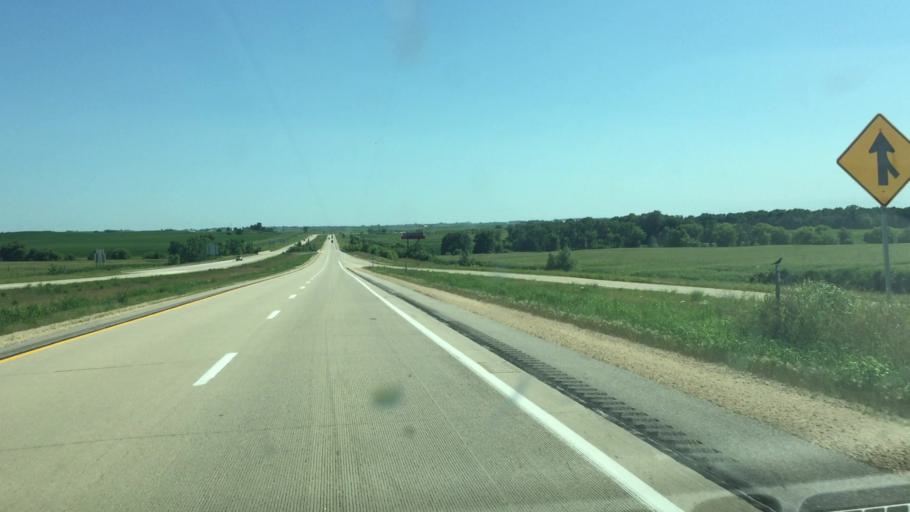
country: US
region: Iowa
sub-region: Jones County
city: Monticello
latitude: 42.2280
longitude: -91.1717
